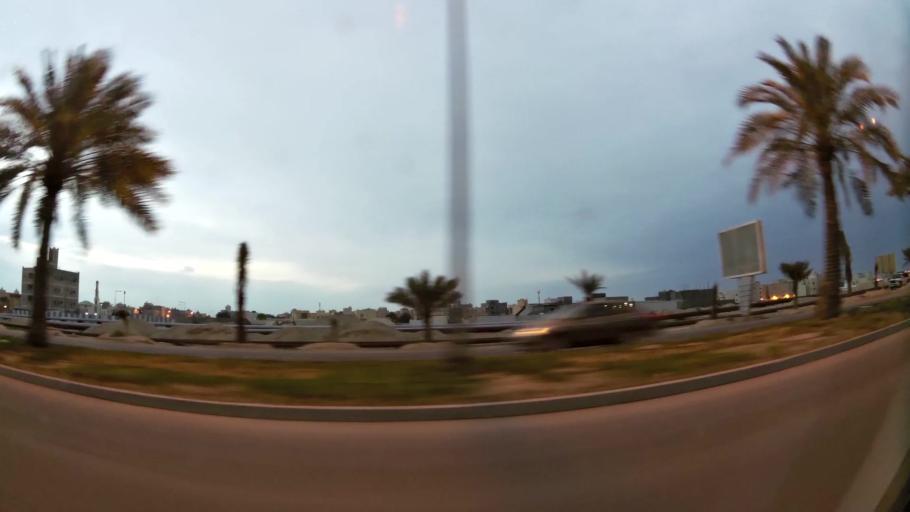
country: BH
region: Central Governorate
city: Madinat Hamad
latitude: 26.1420
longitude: 50.5022
